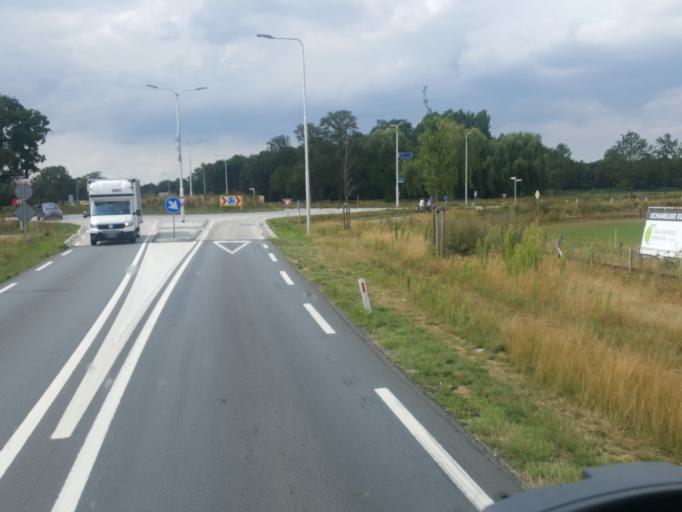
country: NL
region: North Brabant
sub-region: Gemeente Cuijk
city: Cuijk
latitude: 51.6820
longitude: 5.8440
